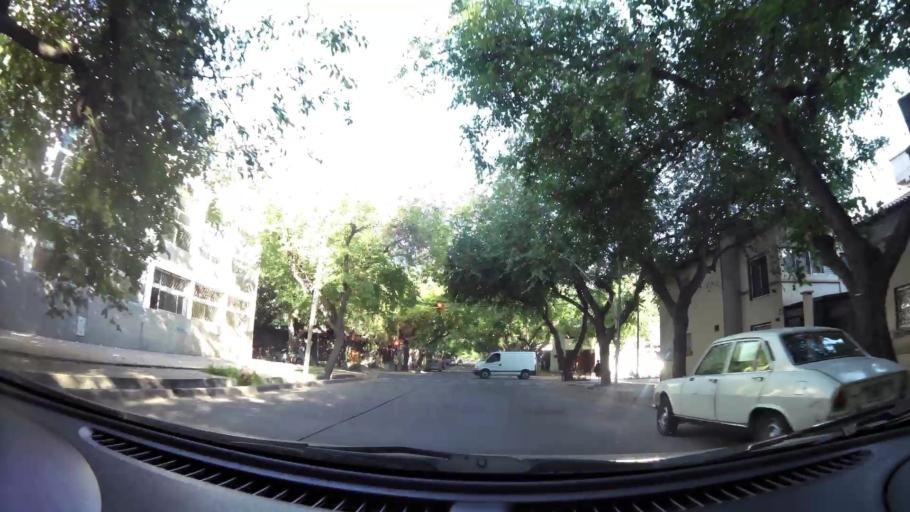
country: AR
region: Mendoza
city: Mendoza
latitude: -32.8735
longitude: -68.8359
